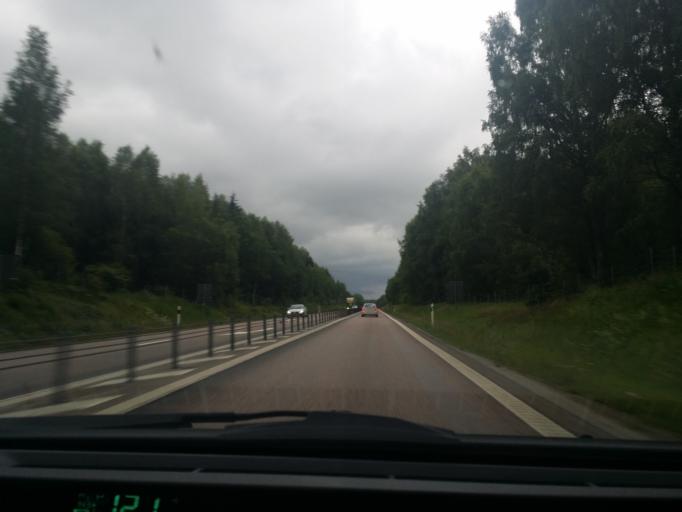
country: SE
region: Vaestmanland
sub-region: Hallstahammars Kommun
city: Kolback
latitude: 59.5861
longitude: 16.2745
